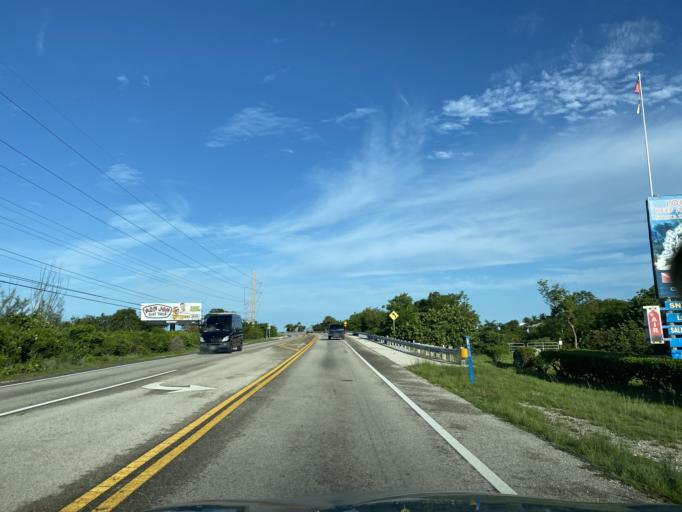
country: US
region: Florida
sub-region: Monroe County
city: Big Pine Key
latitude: 24.6699
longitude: -81.3686
